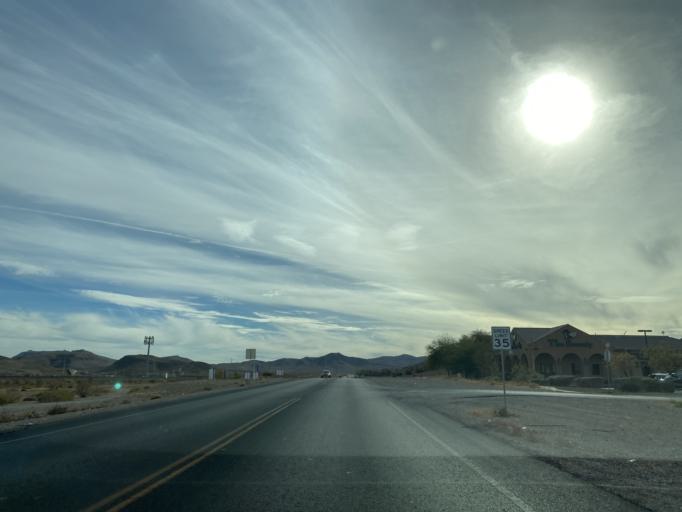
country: US
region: Nevada
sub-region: Clark County
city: Enterprise
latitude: 35.9980
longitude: -115.2436
